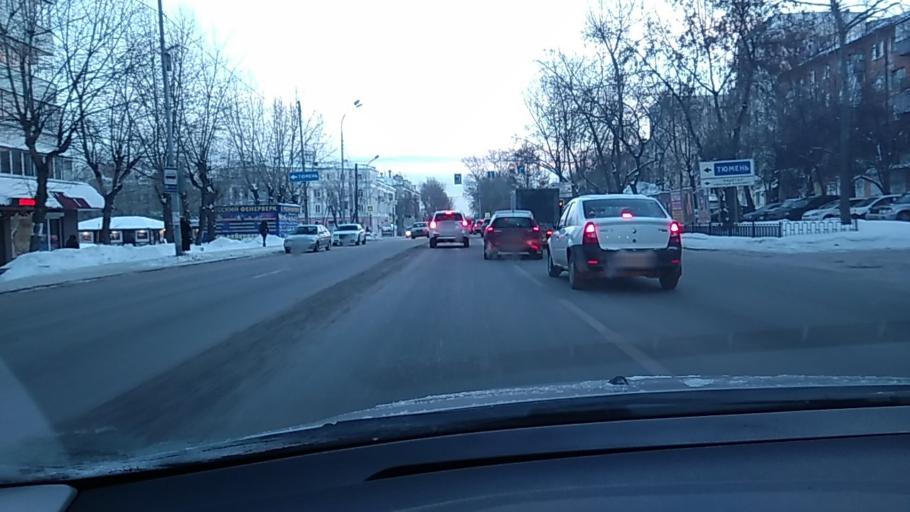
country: RU
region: Sverdlovsk
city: Yekaterinburg
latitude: 56.8271
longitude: 60.6375
